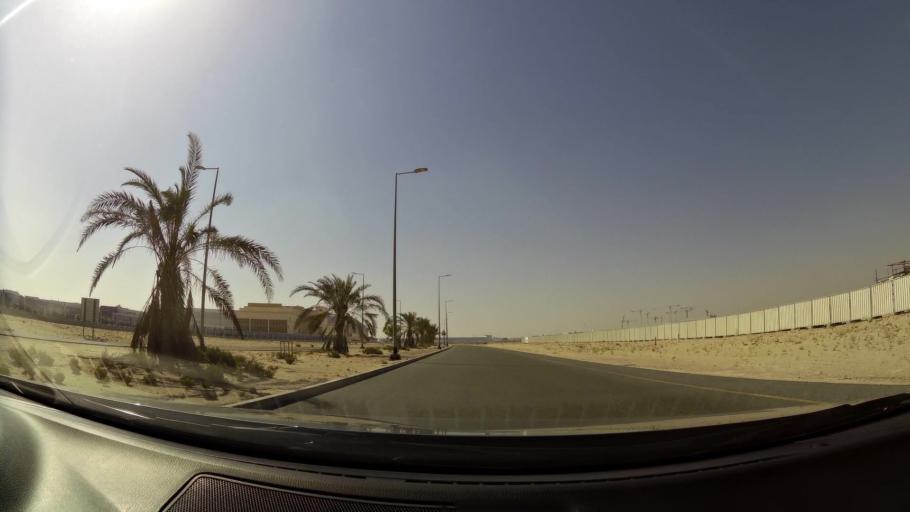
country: AE
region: Dubai
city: Dubai
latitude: 24.9304
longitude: 55.0553
